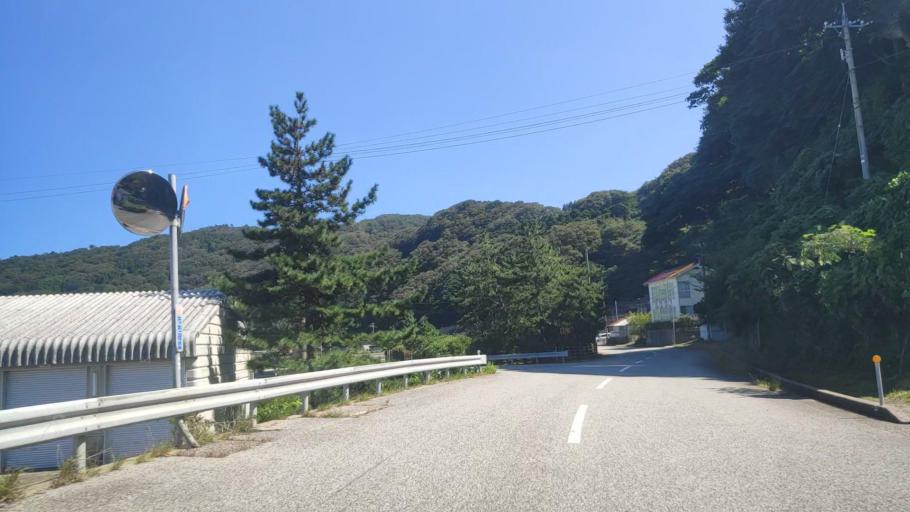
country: JP
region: Ishikawa
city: Nanao
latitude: 37.5193
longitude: 137.2404
